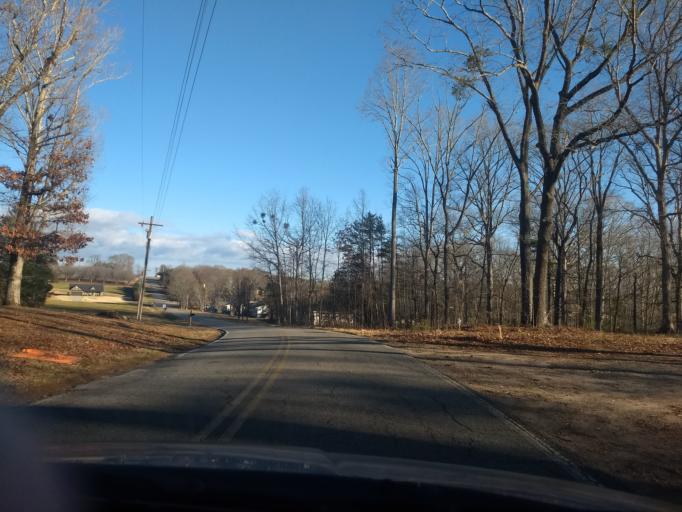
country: US
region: South Carolina
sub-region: Greenville County
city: Greer
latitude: 35.0241
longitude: -82.2017
